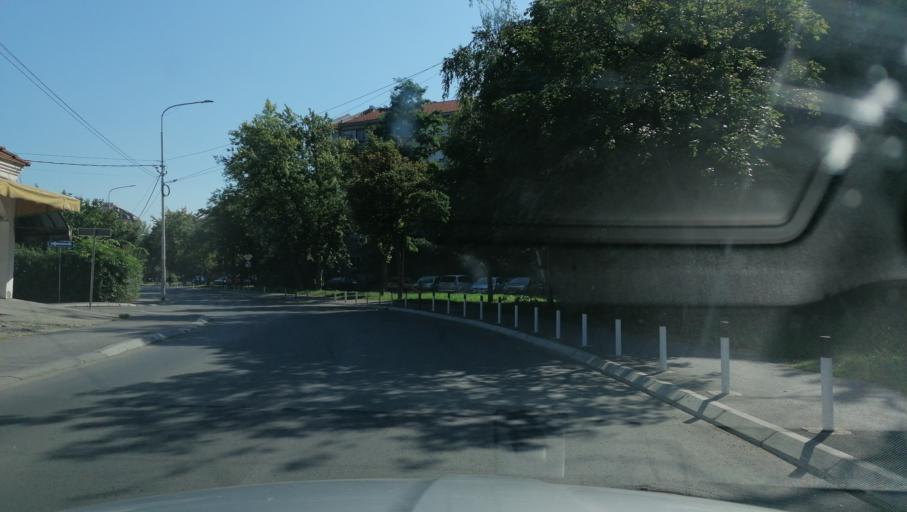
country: RS
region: Central Serbia
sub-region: Rasinski Okrug
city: Krusevac
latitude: 43.5674
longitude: 21.3322
